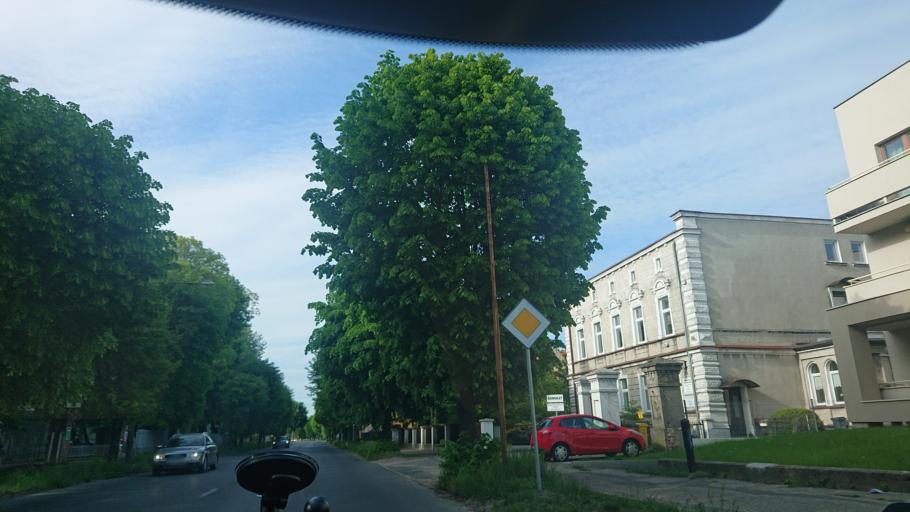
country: PL
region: Greater Poland Voivodeship
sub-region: Powiat gnieznienski
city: Gniezno
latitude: 52.5236
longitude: 17.5970
